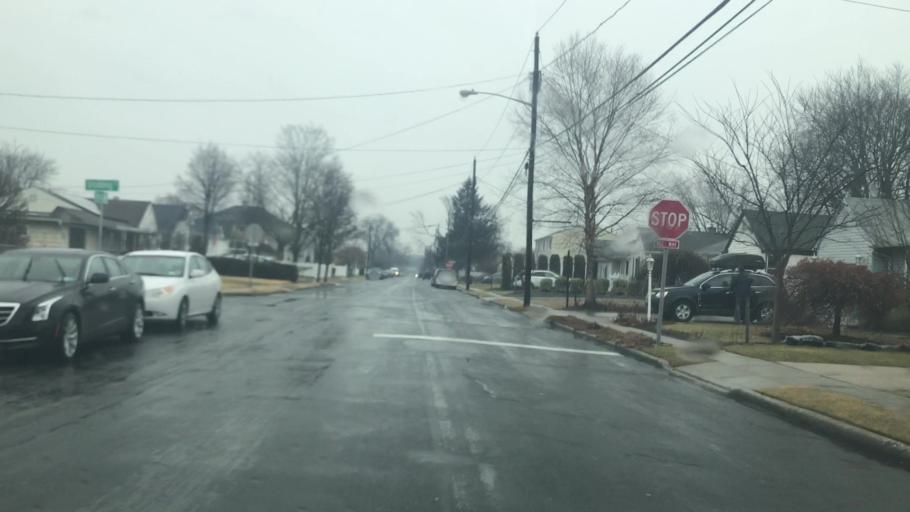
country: US
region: New York
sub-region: Suffolk County
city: North Lindenhurst
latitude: 40.7107
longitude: -73.3791
